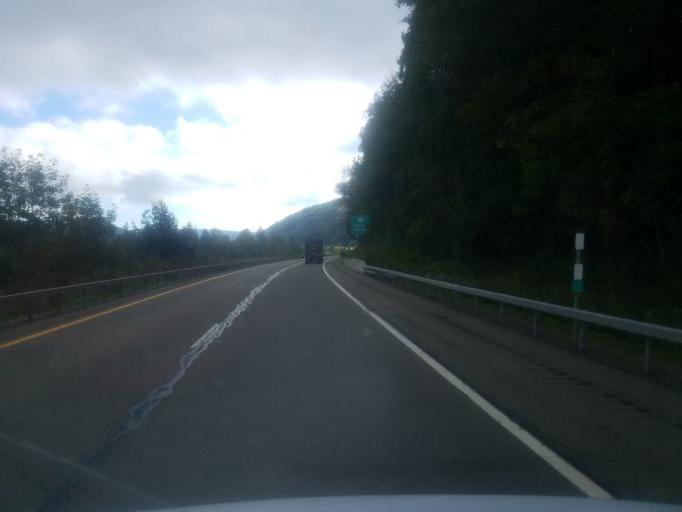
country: US
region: New York
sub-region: Cattaraugus County
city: Salamanca
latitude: 42.1496
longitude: -78.7159
